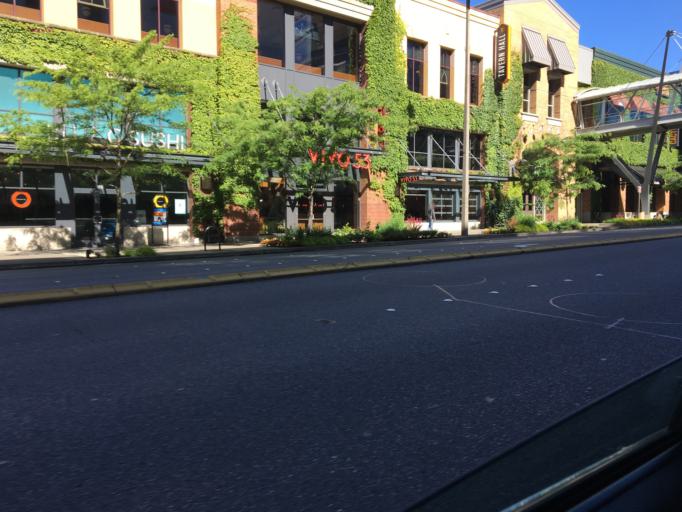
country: US
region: Washington
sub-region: King County
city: Bellevue
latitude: 47.6162
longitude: -122.2016
